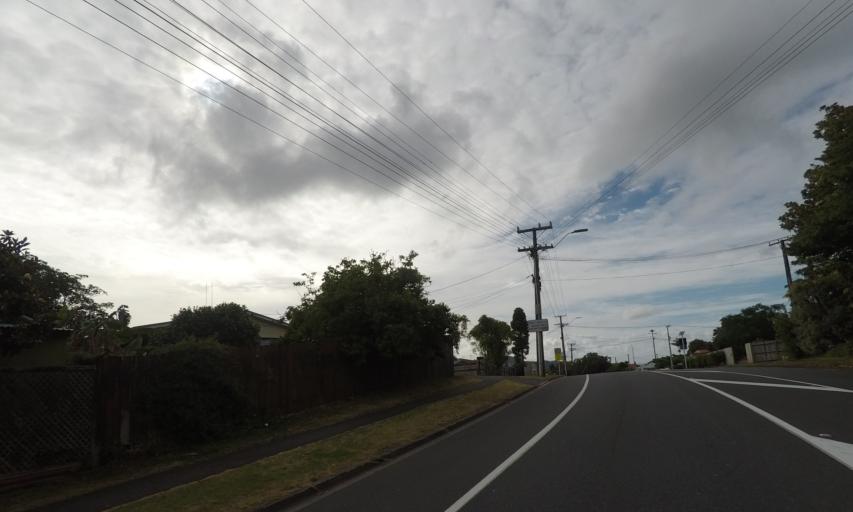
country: NZ
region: Northland
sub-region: Whangarei
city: Whangarei
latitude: -35.6891
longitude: 174.3042
